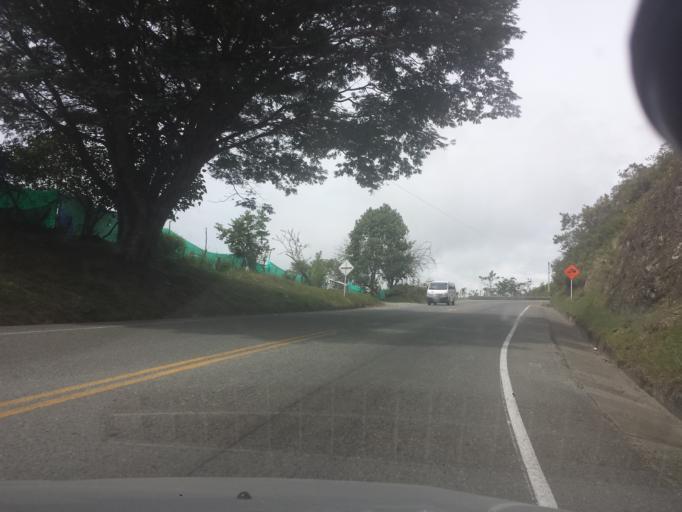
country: CO
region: Antioquia
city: Antioquia
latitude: 6.6058
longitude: -75.8558
